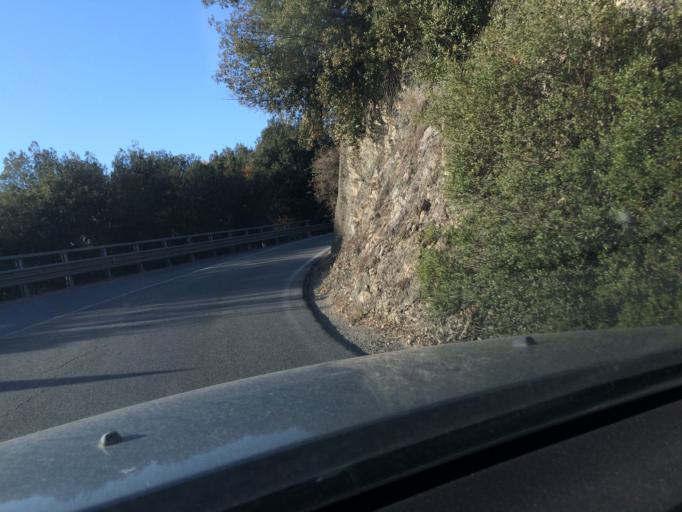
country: IT
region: Umbria
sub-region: Provincia di Terni
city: Fornole
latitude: 42.5512
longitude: 12.4447
